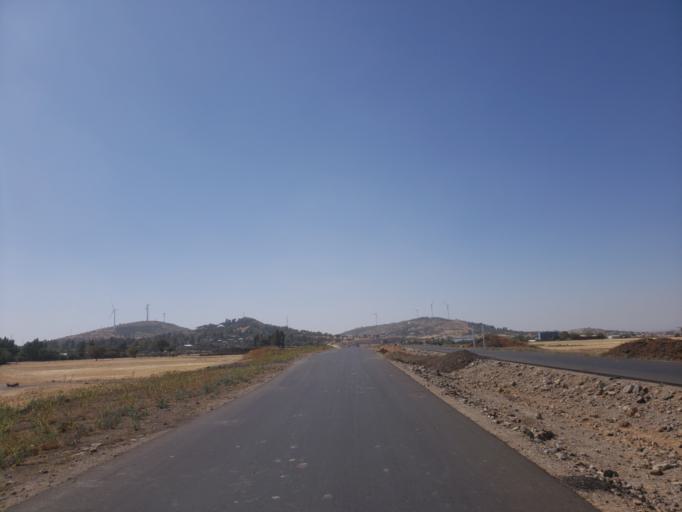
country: ET
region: Oromiya
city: Mojo
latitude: 8.5748
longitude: 39.1700
